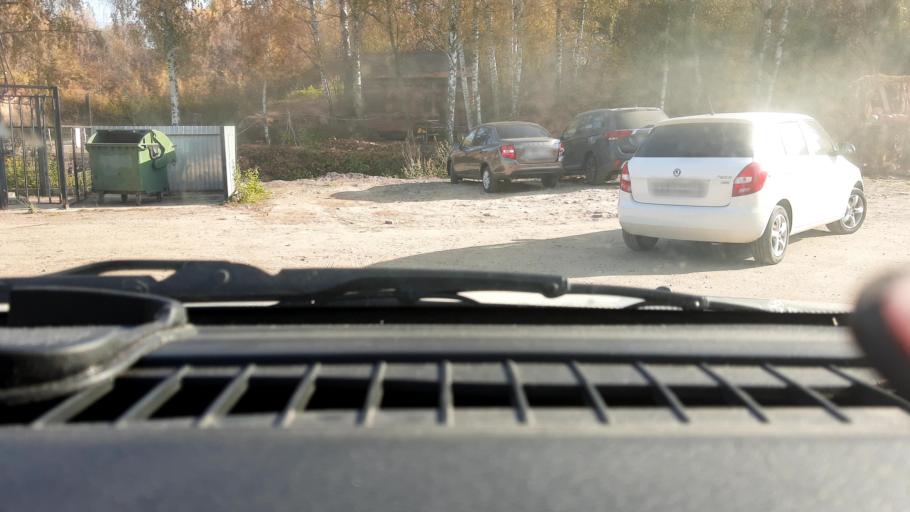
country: RU
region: Nizjnij Novgorod
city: Afonino
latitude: 56.2310
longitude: 44.0937
